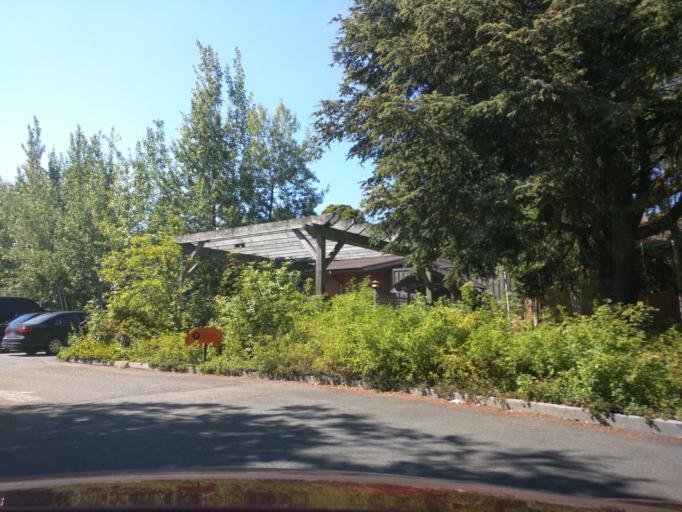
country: US
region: Washington
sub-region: King County
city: Seattle
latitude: 47.6659
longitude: -122.3500
